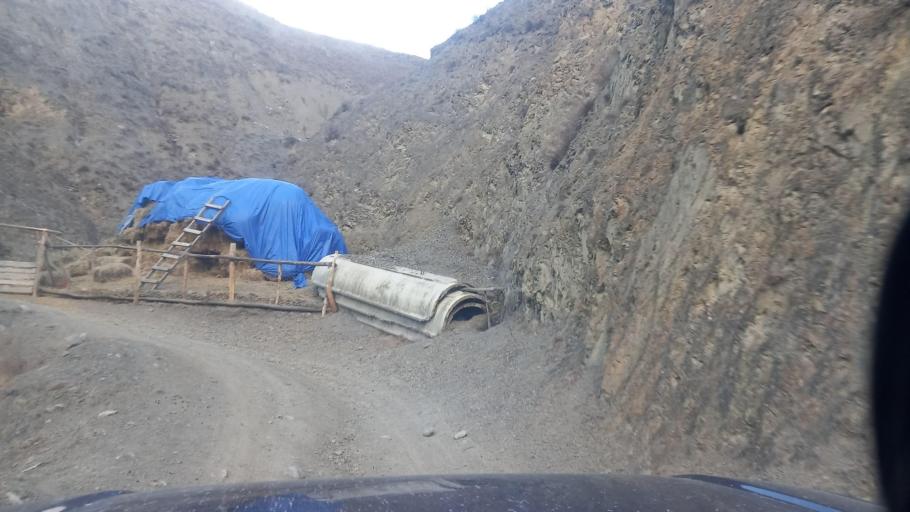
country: RU
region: Ingushetiya
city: Dzhayrakh
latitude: 42.8032
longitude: 44.7547
